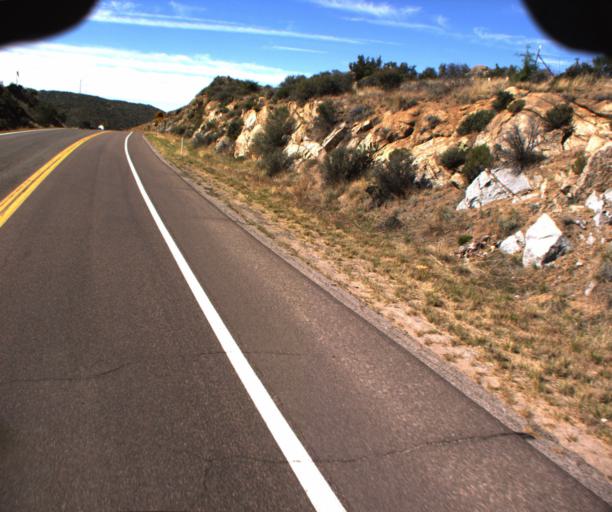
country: US
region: Arizona
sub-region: Yavapai County
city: Congress
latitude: 34.2116
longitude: -112.7554
